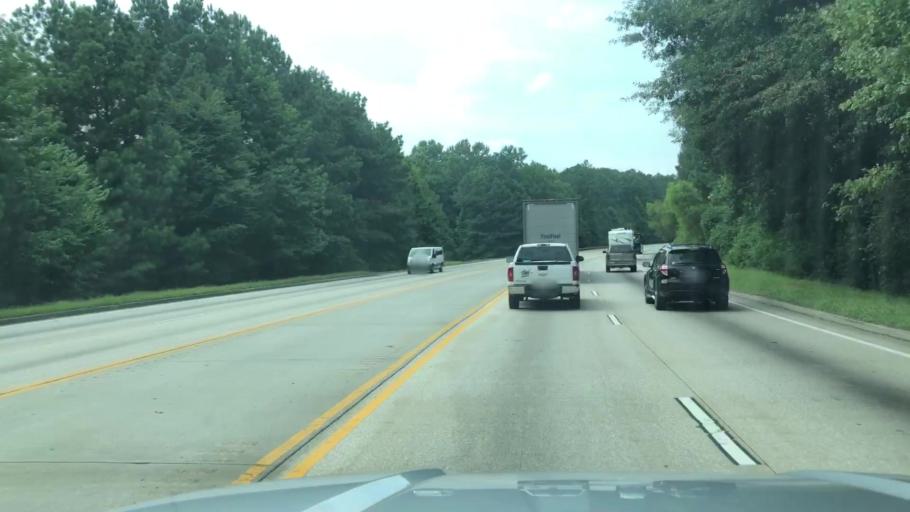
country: US
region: Georgia
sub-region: Douglas County
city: Lithia Springs
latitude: 33.7989
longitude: -84.6472
